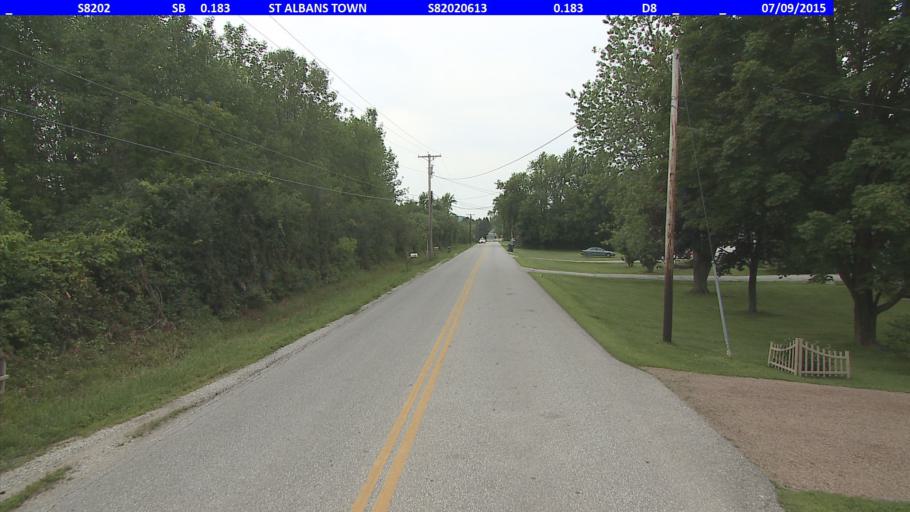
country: US
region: Vermont
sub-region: Franklin County
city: Saint Albans
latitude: 44.8146
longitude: -73.1074
